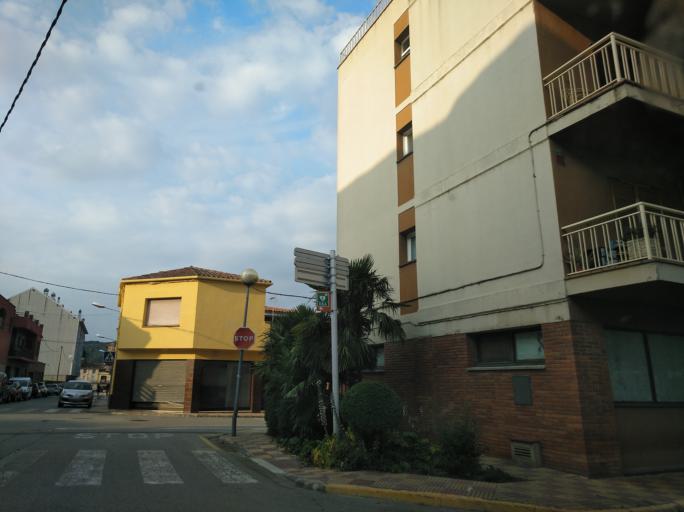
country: ES
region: Catalonia
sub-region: Provincia de Girona
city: la Cellera de Ter
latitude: 41.9672
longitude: 2.6220
